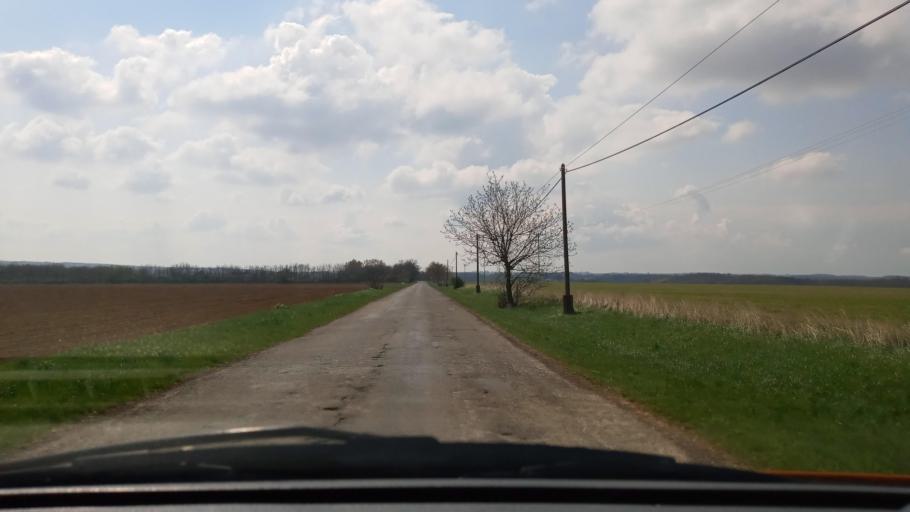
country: HU
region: Baranya
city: Pecsvarad
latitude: 46.0880
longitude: 18.5041
